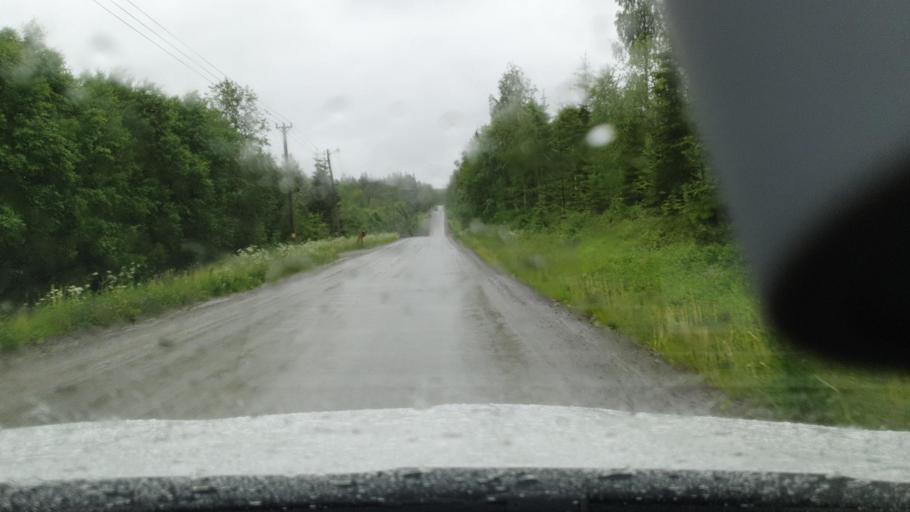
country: SE
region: Vaesterbotten
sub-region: Skelleftea Kommun
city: Burtraesk
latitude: 64.3558
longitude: 20.4759
